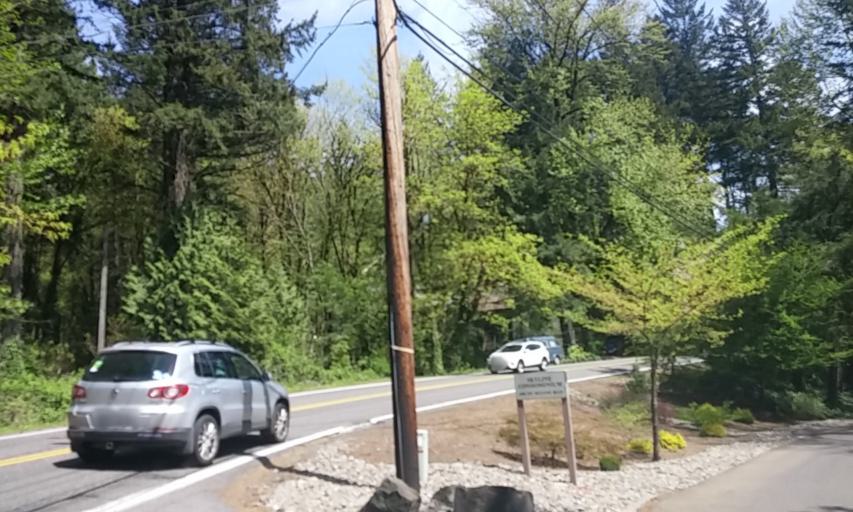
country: US
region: Oregon
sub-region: Washington County
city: West Slope
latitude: 45.5117
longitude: -122.7322
